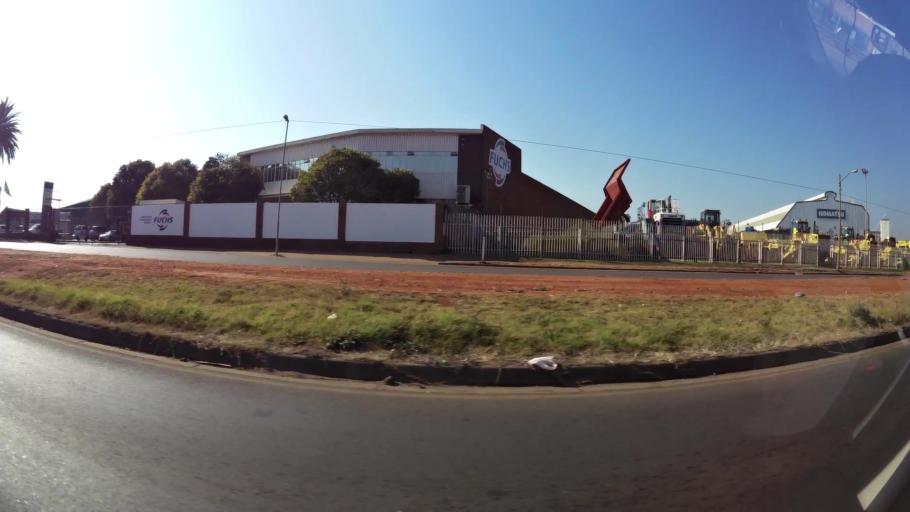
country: ZA
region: Gauteng
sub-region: City of Johannesburg Metropolitan Municipality
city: Modderfontein
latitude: -26.1463
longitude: 28.2019
